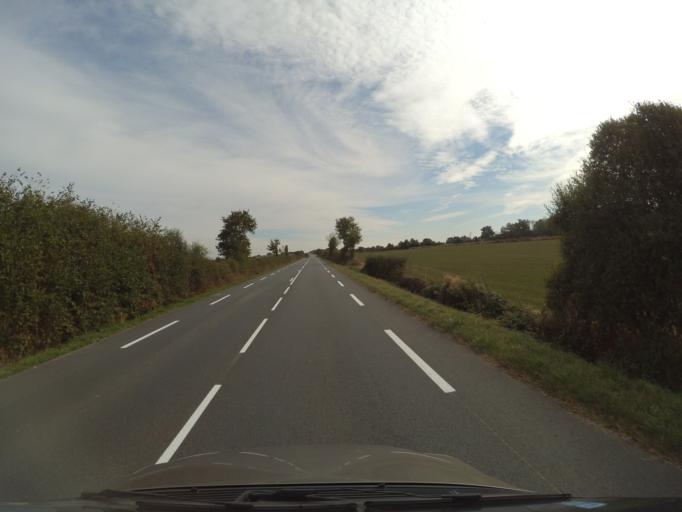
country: FR
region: Pays de la Loire
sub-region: Departement de Maine-et-Loire
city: Chemille-Melay
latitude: 47.2127
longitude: -0.7757
